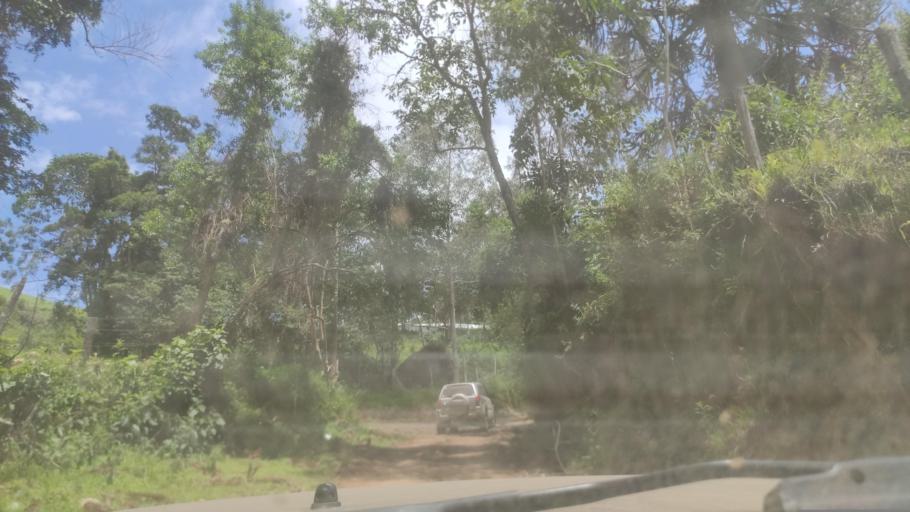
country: BR
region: Minas Gerais
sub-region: Cambui
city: Cambui
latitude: -22.6679
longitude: -45.9464
